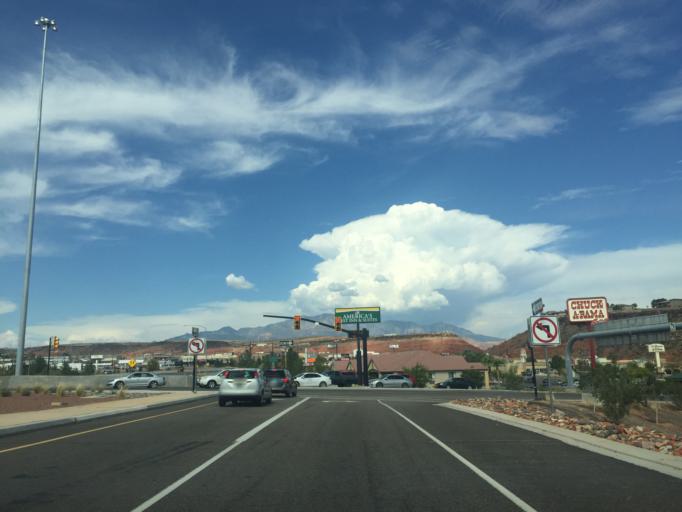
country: US
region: Utah
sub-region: Washington County
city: Saint George
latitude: 37.1093
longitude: -113.5565
